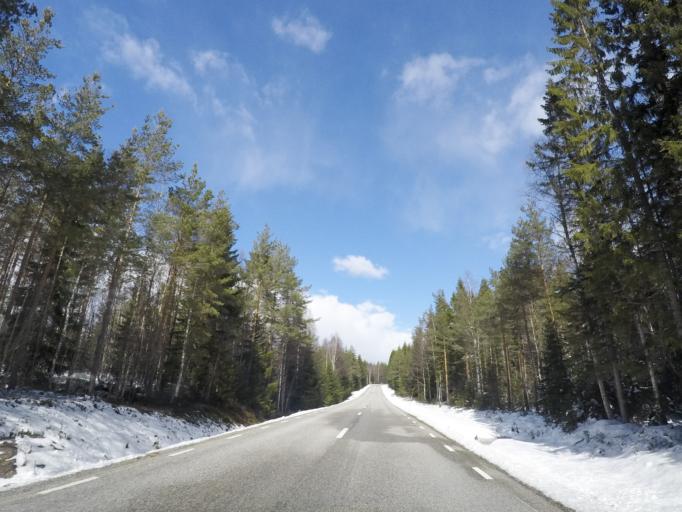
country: SE
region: OErebro
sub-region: Lindesbergs Kommun
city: Stora
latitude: 59.8985
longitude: 15.1903
